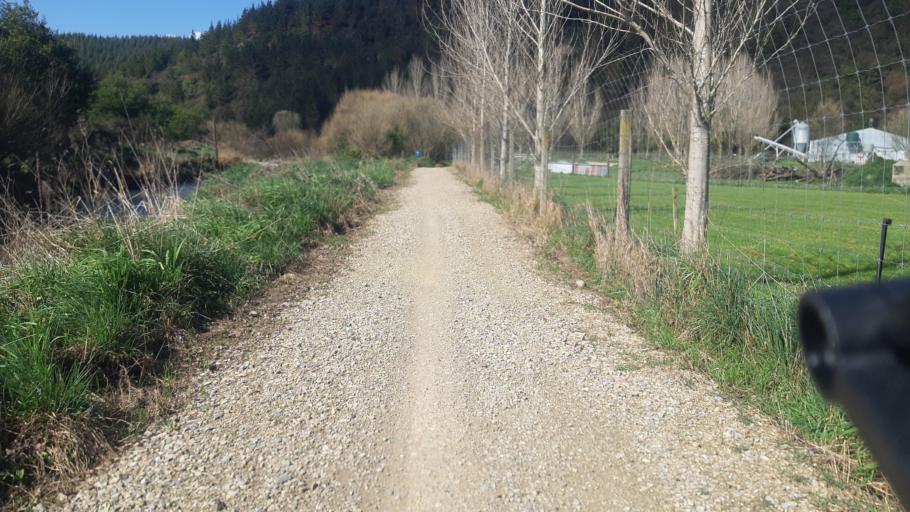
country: NZ
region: Tasman
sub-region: Tasman District
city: Wakefield
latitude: -41.4464
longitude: 172.9729
